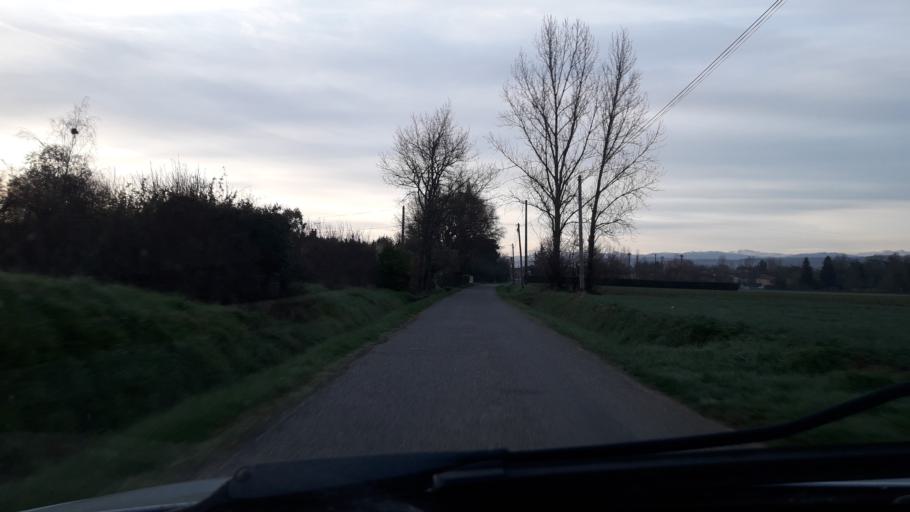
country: FR
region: Midi-Pyrenees
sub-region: Departement de la Haute-Garonne
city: Montesquieu-Volvestre
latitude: 43.1709
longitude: 1.2722
